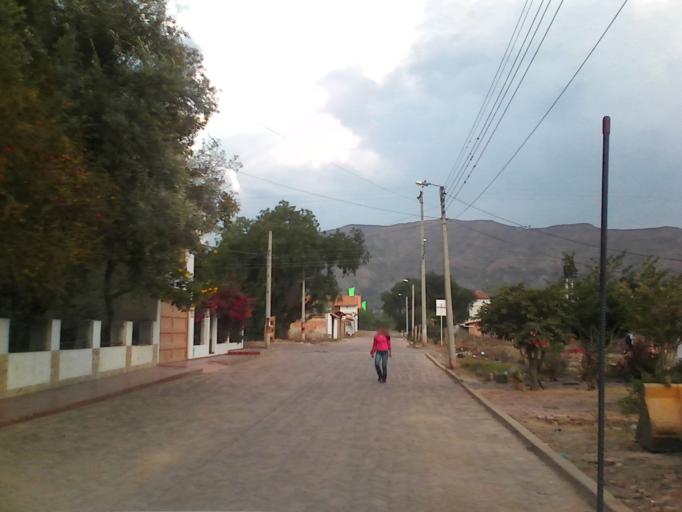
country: CO
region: Boyaca
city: Sachica
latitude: 5.5838
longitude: -73.5432
